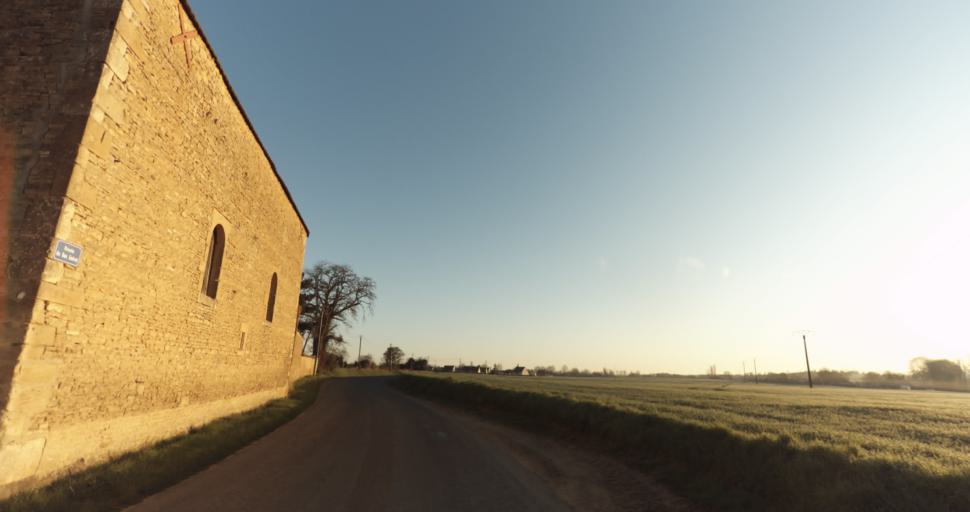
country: FR
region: Lower Normandy
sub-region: Departement du Calvados
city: Saint-Pierre-sur-Dives
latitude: 49.0292
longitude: -0.0317
